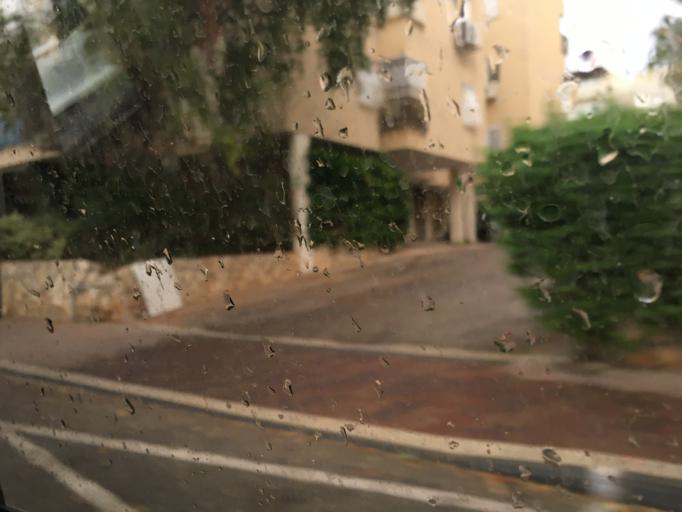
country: IL
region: Tel Aviv
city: Ramat HaSharon
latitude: 32.1418
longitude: 34.8386
